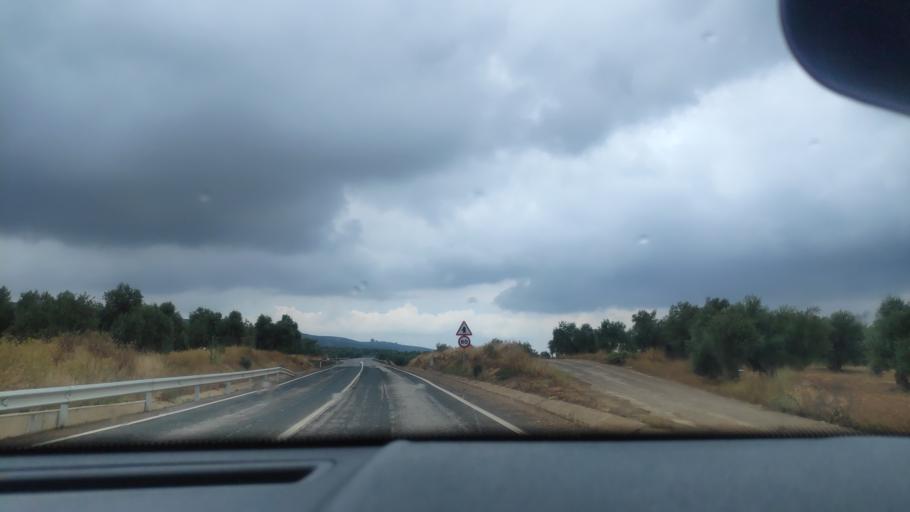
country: ES
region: Andalusia
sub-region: Provincia de Jaen
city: Jabalquinto
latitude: 38.0442
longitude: -3.7324
